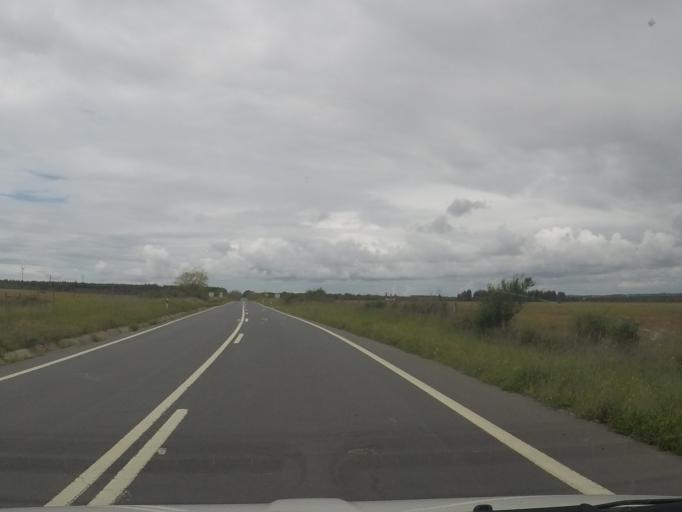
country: PT
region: Setubal
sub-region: Santiago do Cacem
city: Cercal
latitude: 37.8401
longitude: -8.7036
